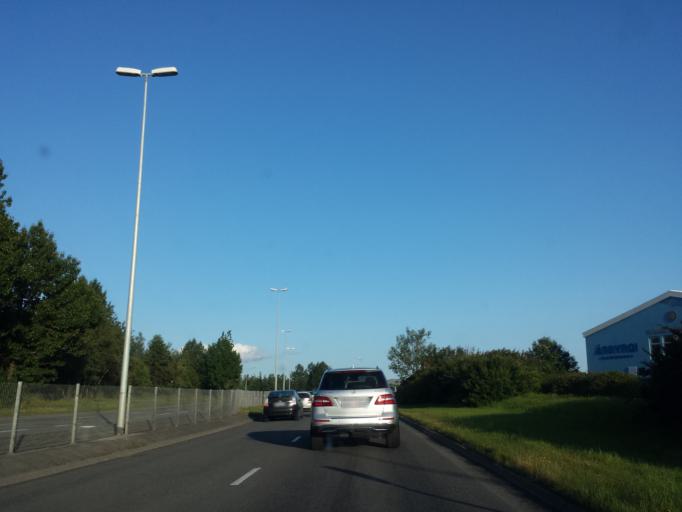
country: IS
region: Capital Region
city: Reykjavik
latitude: 64.1314
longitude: -21.8658
